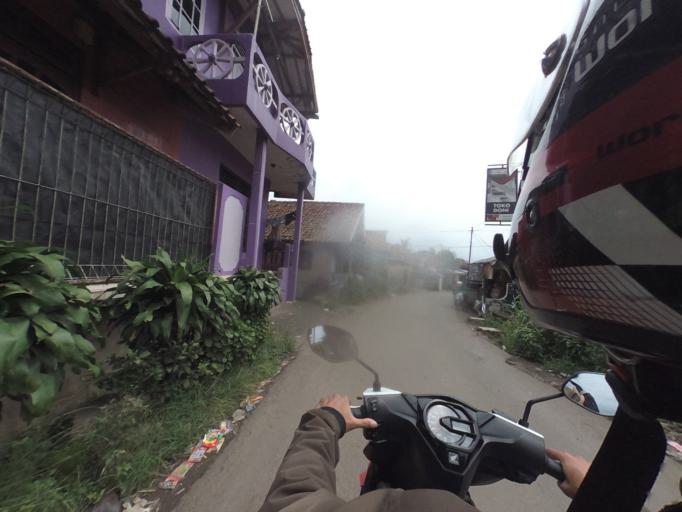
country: ID
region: West Java
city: Bogor
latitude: -6.6088
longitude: 106.7567
